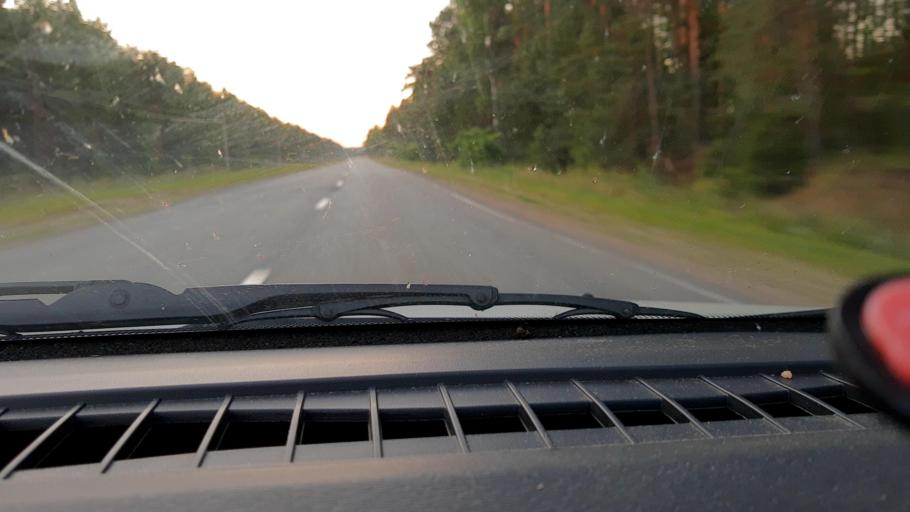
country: RU
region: Nizjnij Novgorod
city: Uren'
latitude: 57.4135
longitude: 45.6847
